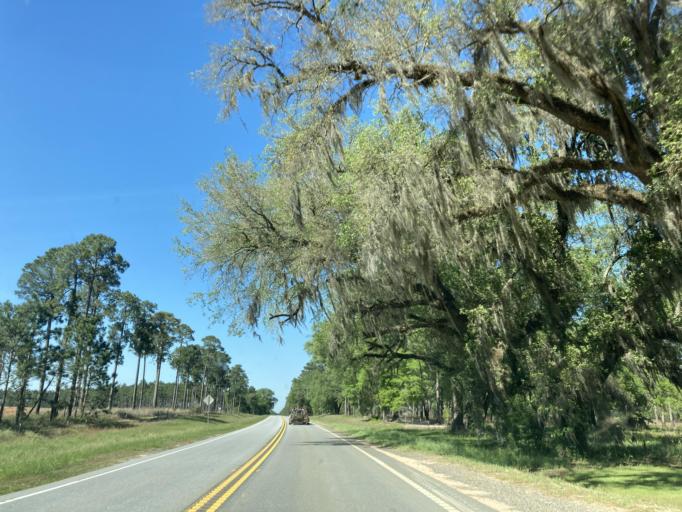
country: US
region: Georgia
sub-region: Baker County
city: Newton
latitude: 31.3743
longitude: -84.2845
